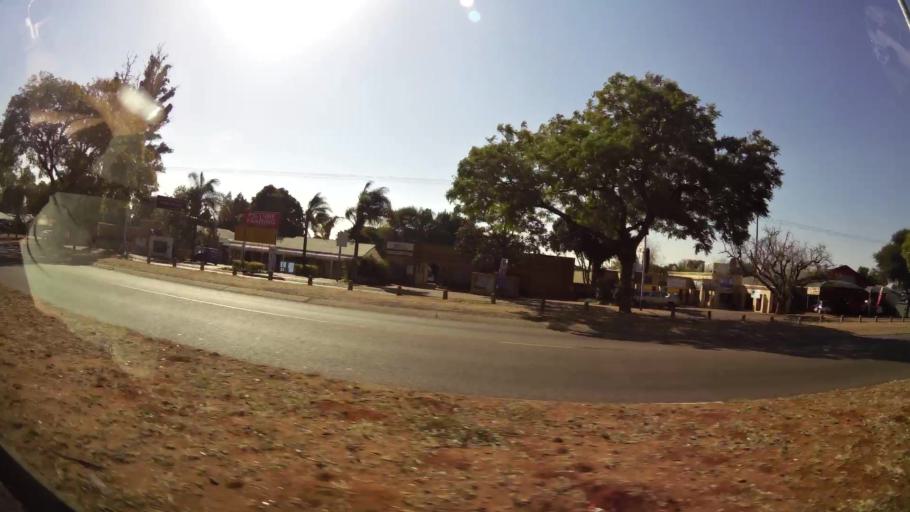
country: ZA
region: Gauteng
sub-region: City of Tshwane Metropolitan Municipality
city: Pretoria
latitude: -25.6813
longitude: 28.2212
